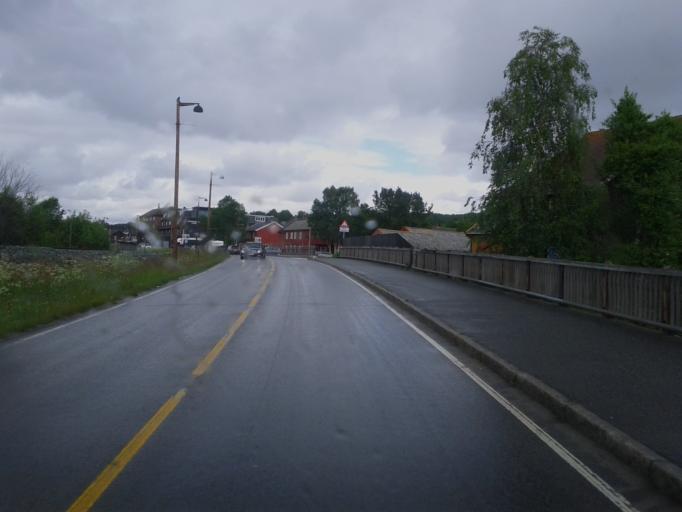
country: NO
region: Sor-Trondelag
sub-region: Roros
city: Roros
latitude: 62.5726
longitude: 11.3868
